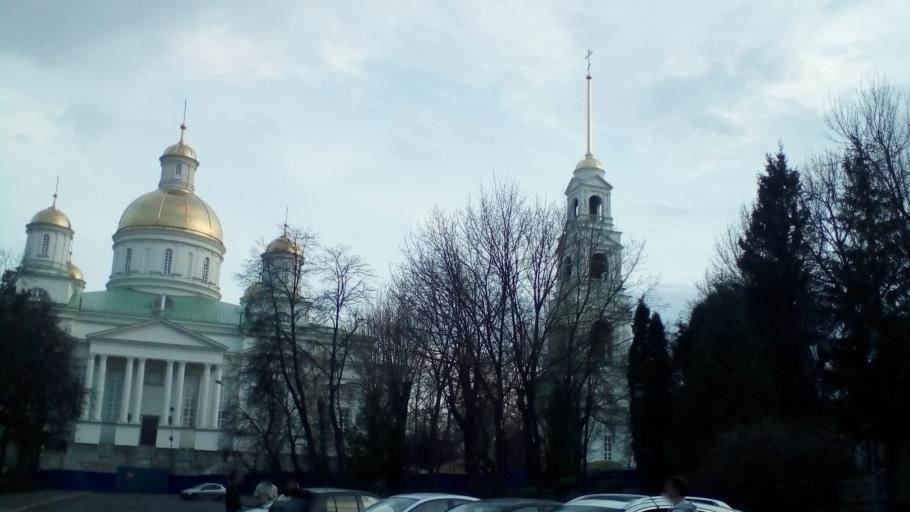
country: RU
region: Penza
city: Penza
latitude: 53.1852
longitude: 45.0139
